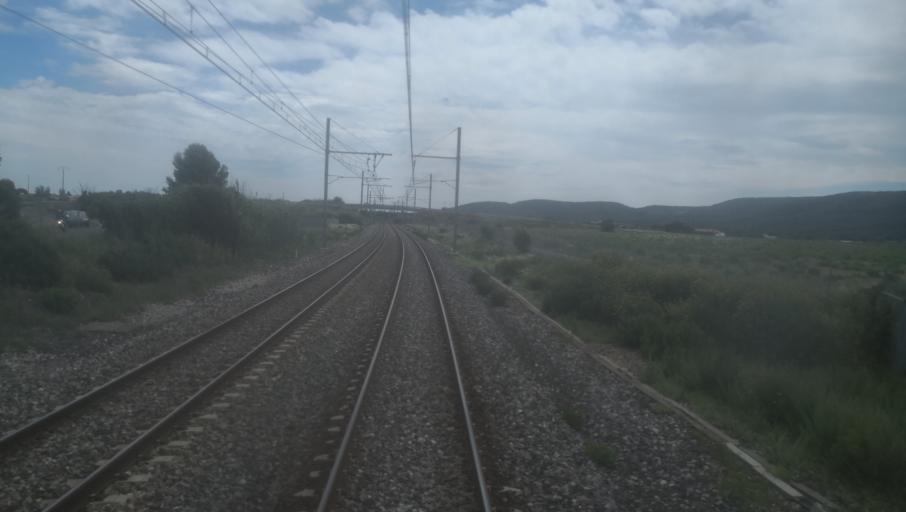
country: FR
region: Languedoc-Roussillon
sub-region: Departement de l'Herault
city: Vic-la-Gardiole
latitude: 43.4980
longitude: 3.7960
